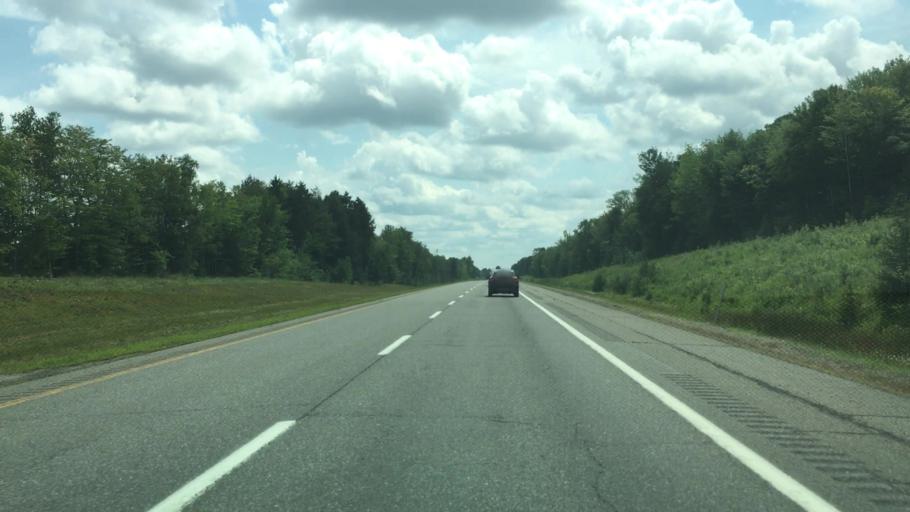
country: US
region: Maine
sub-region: Penobscot County
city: Howland
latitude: 45.3067
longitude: -68.6606
